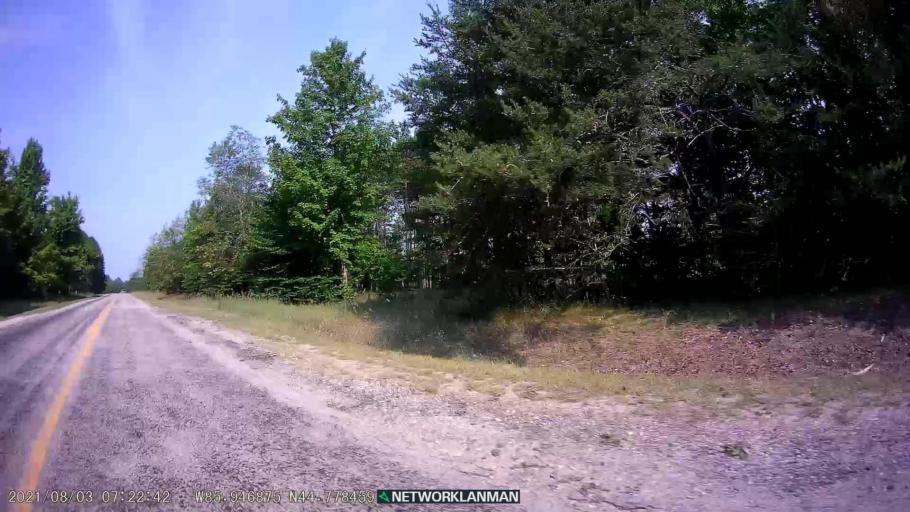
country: US
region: Michigan
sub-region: Benzie County
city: Beulah
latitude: 44.7785
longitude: -85.9473
